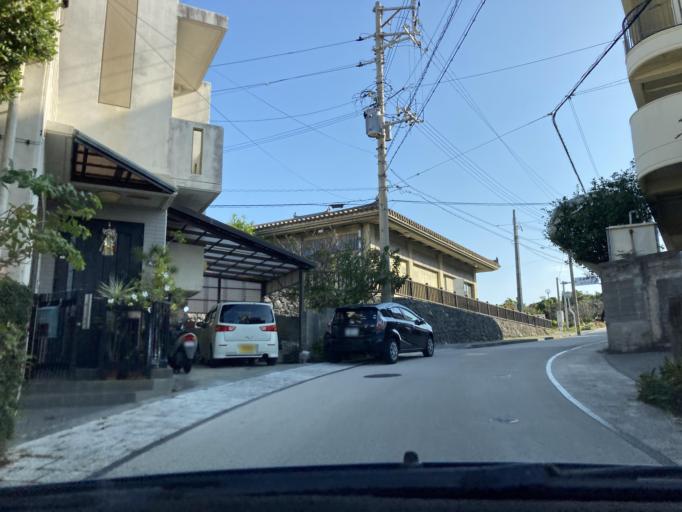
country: JP
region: Okinawa
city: Ginowan
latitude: 26.2486
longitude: 127.7286
